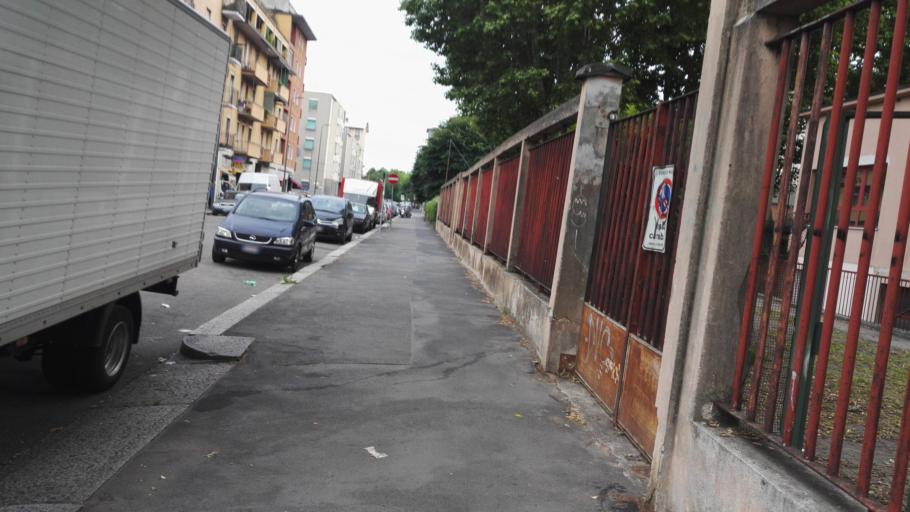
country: IT
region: Lombardy
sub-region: Citta metropolitana di Milano
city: Chiaravalle
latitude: 45.4528
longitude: 9.2268
